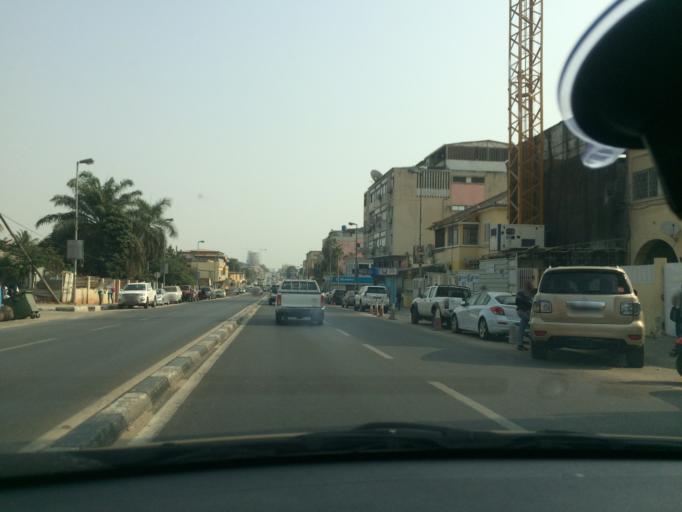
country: AO
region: Luanda
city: Luanda
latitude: -8.8271
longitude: 13.2231
